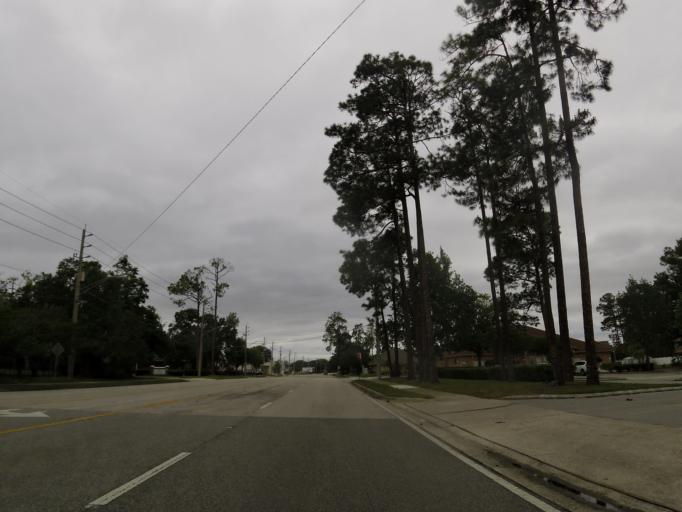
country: US
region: Florida
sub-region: Saint Johns County
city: Fruit Cove
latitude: 30.1985
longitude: -81.6143
